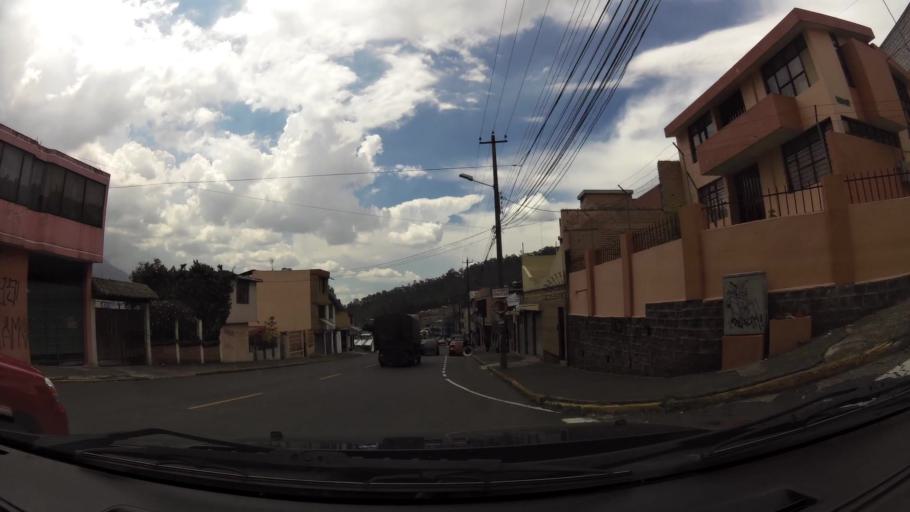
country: EC
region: Pichincha
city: Quito
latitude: -0.2461
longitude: -78.5070
